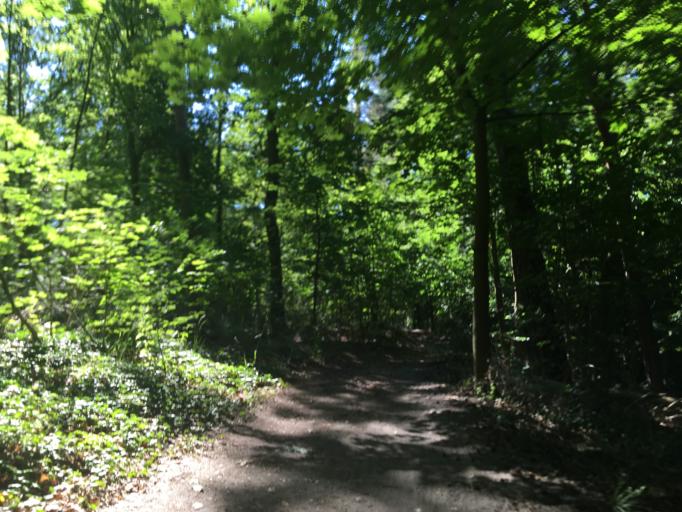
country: DE
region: Brandenburg
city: Erkner
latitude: 52.4277
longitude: 13.7636
